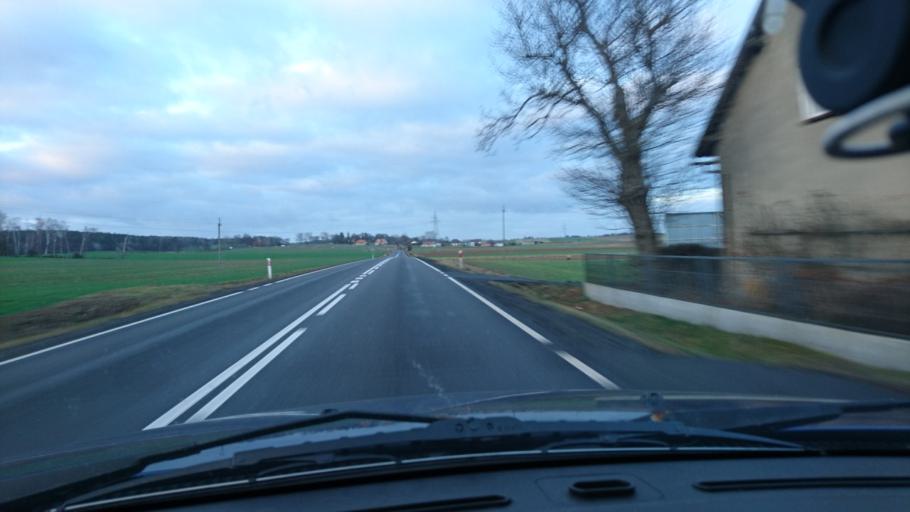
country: PL
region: Greater Poland Voivodeship
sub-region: Powiat ostrzeszowski
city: Ostrzeszow
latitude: 51.3601
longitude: 17.9465
